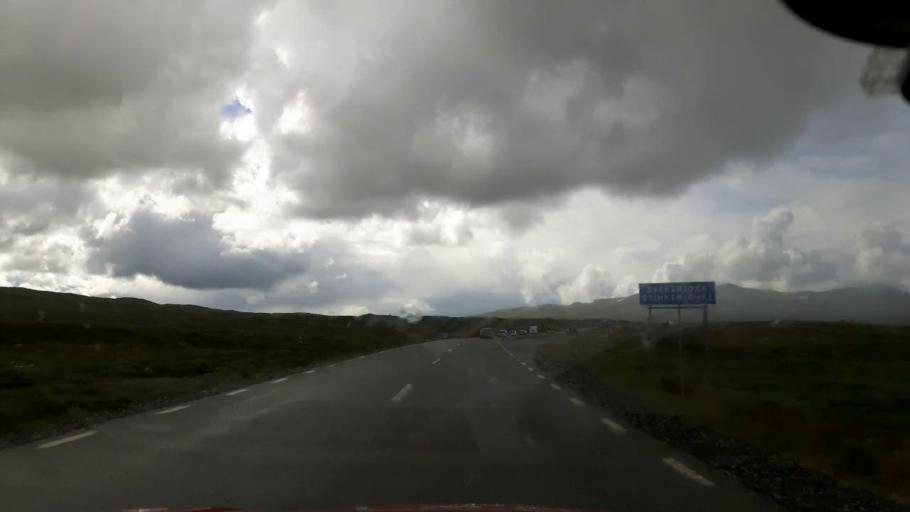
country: NO
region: Nordland
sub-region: Hattfjelldal
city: Hattfjelldal
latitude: 65.0971
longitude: 14.4669
